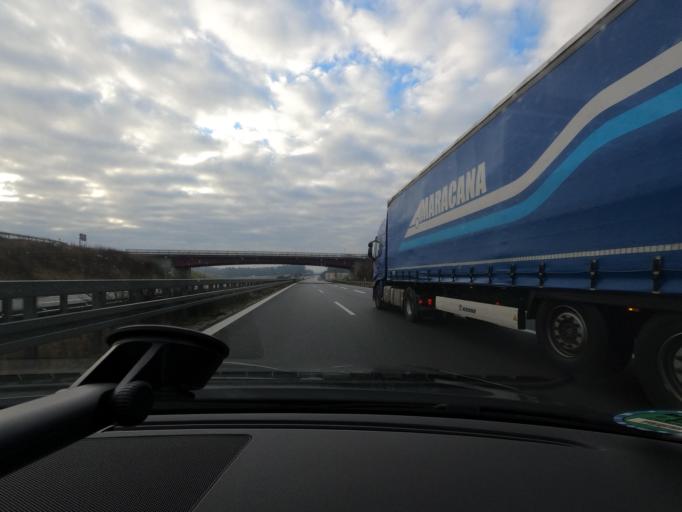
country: DE
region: Bavaria
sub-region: Upper Franconia
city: Niederfullbach
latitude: 50.2228
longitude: 11.0498
